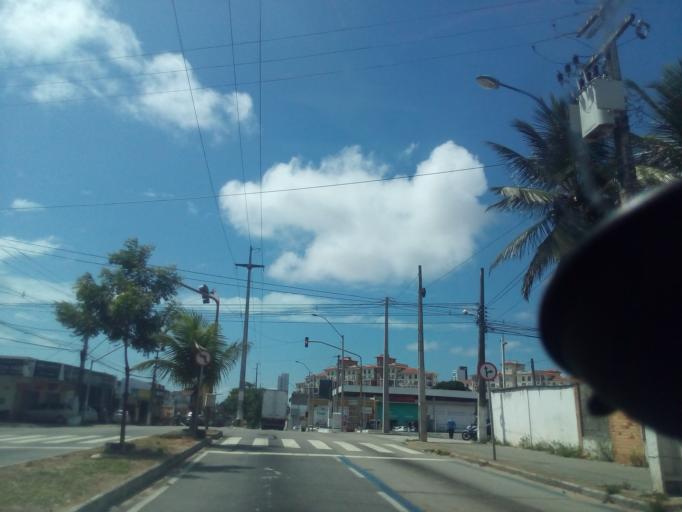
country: BR
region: Rio Grande do Norte
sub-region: Natal
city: Natal
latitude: -5.8223
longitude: -35.2305
